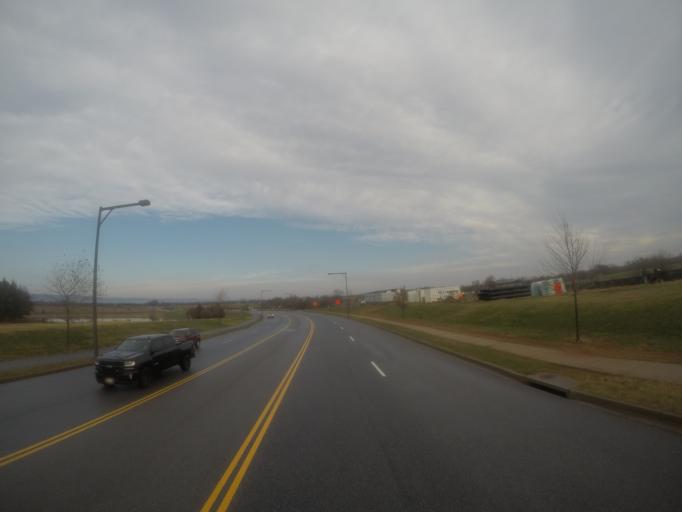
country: US
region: Maryland
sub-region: Frederick County
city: Frederick
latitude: 39.4223
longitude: -77.3835
